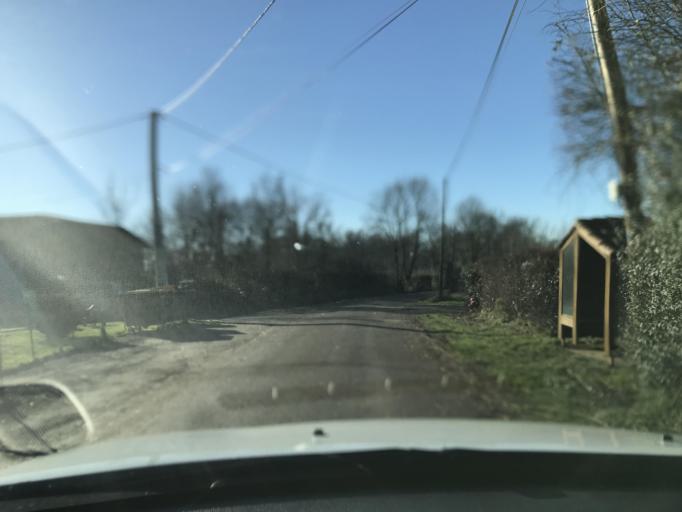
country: FR
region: Poitou-Charentes
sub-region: Departement de la Charente
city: Loubert
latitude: 45.8464
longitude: 0.5436
